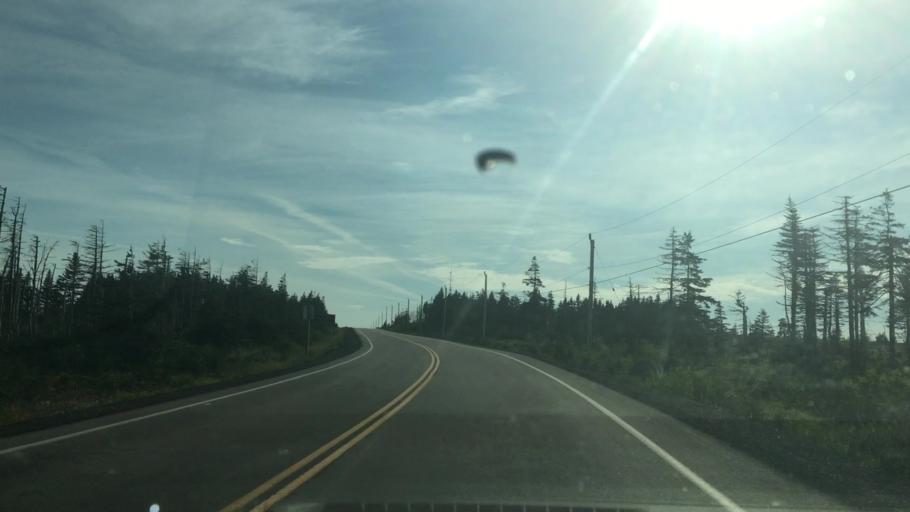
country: CA
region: Nova Scotia
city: Sydney Mines
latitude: 46.8228
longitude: -60.6620
